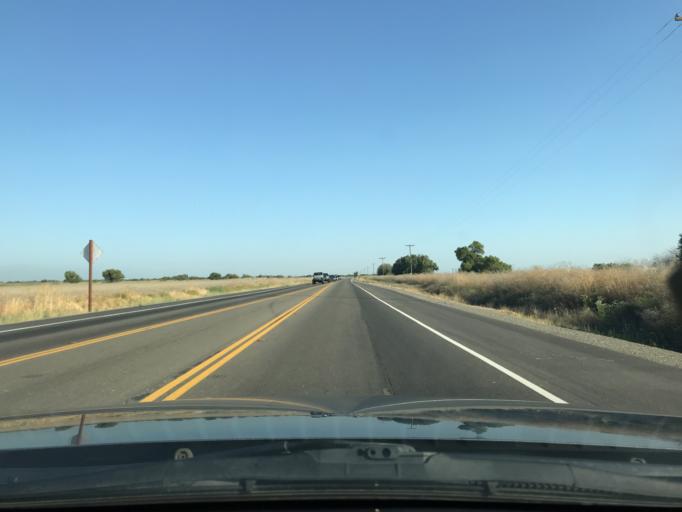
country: US
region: California
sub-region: Merced County
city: Los Banos
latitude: 37.1910
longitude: -120.8389
